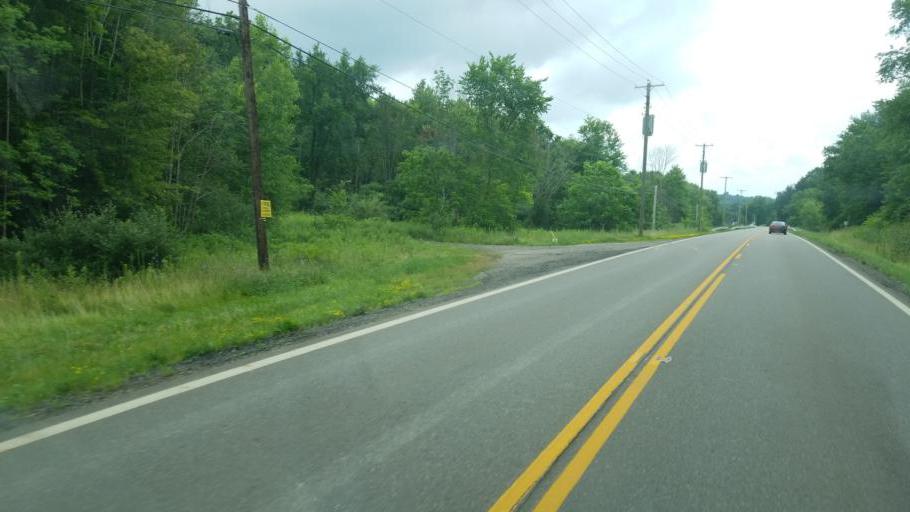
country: US
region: Ohio
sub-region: Columbiana County
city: Lisbon
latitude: 40.7520
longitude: -80.7875
